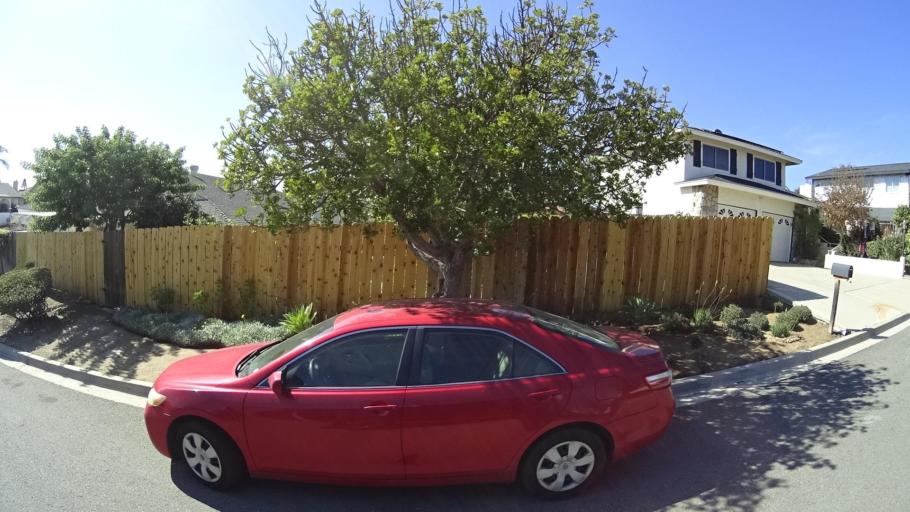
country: US
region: California
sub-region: San Diego County
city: Casa de Oro-Mount Helix
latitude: 32.7578
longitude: -116.9811
